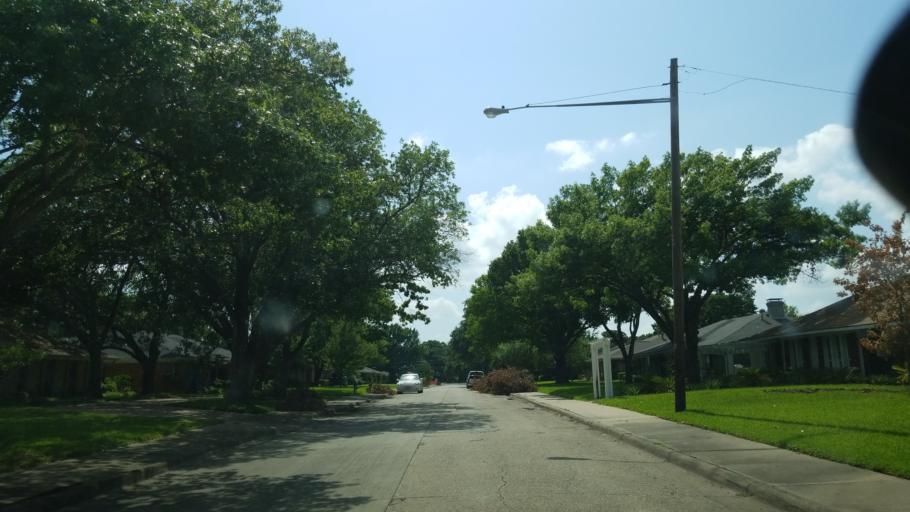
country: US
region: Texas
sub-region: Dallas County
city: Farmers Branch
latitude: 32.8821
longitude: -96.8632
